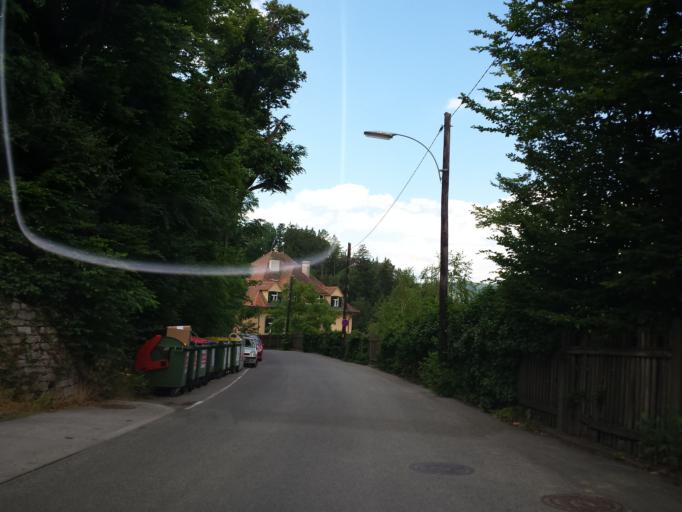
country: AT
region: Styria
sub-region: Graz Stadt
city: Graz
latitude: 47.0928
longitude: 15.4368
